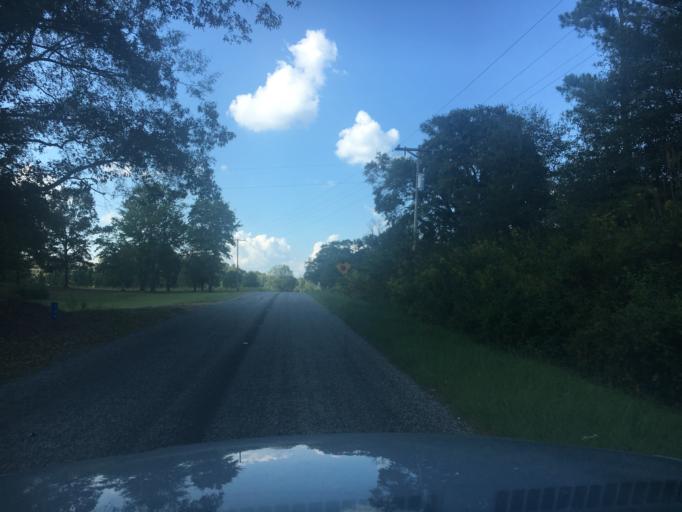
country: US
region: South Carolina
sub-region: Greenwood County
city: Ware Shoals
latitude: 34.5023
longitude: -82.2329
